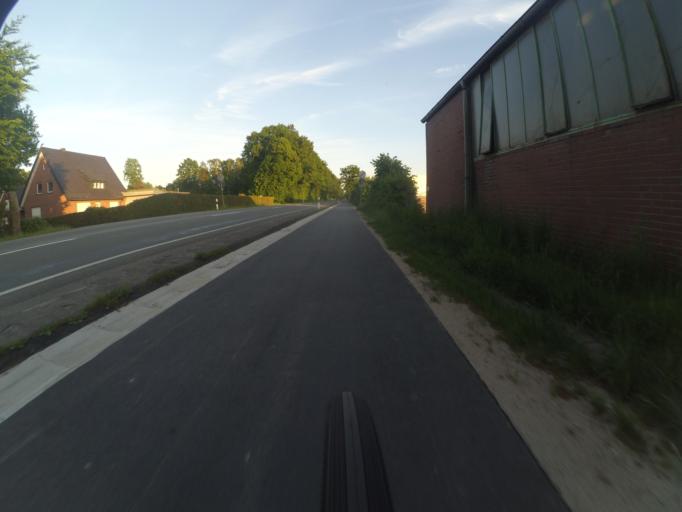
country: DE
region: North Rhine-Westphalia
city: Ibbenburen
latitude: 52.3254
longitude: 7.6689
